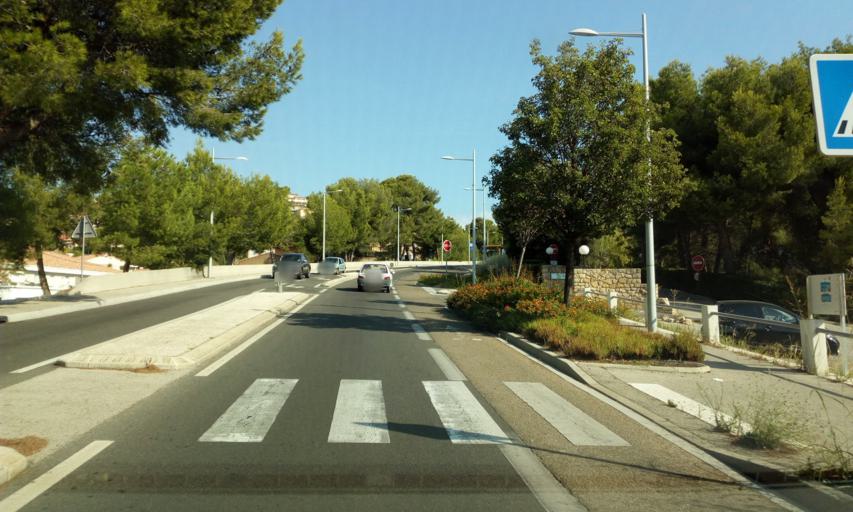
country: FR
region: Provence-Alpes-Cote d'Azur
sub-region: Departement du Var
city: Bandol
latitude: 43.1433
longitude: 5.7477
